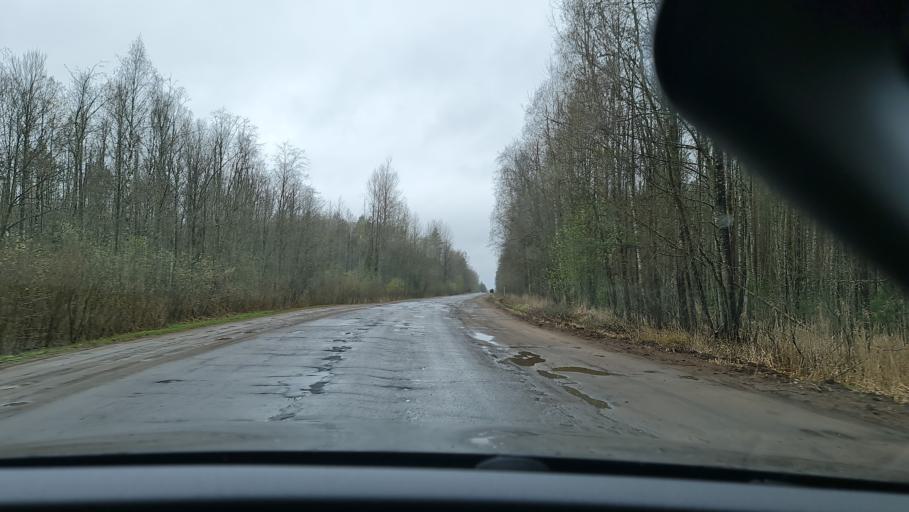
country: RU
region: Novgorod
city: Demyansk
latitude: 57.6758
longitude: 32.5517
